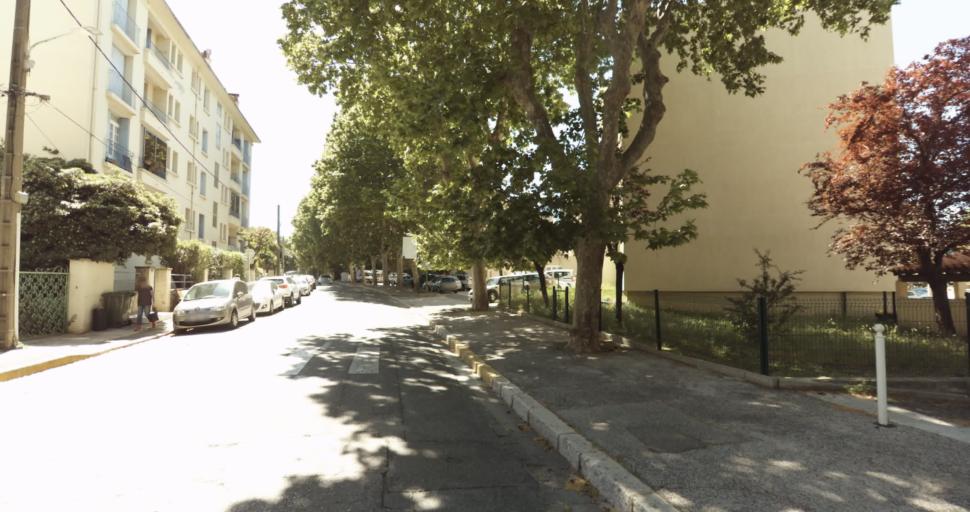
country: FR
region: Provence-Alpes-Cote d'Azur
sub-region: Departement du Var
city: Toulon
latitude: 43.1144
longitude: 5.9446
